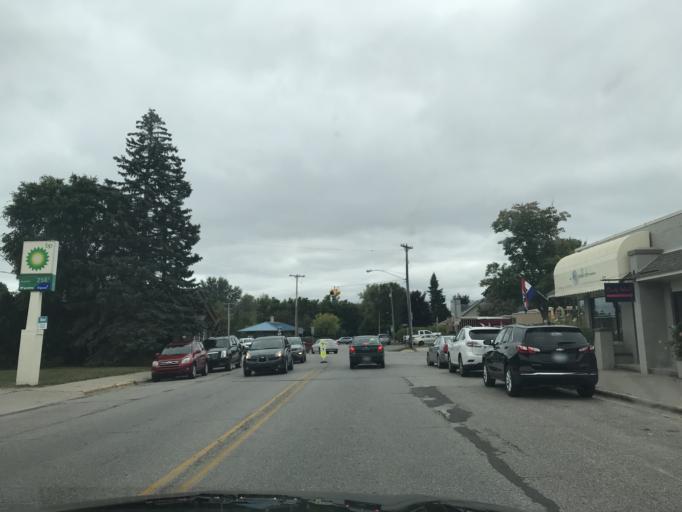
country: US
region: Michigan
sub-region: Leelanau County
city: Leland
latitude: 44.9748
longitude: -85.6512
